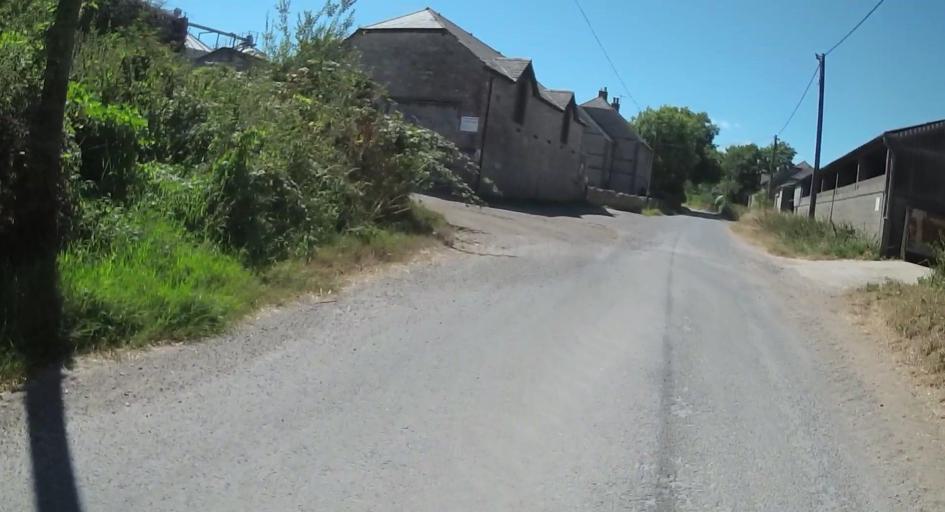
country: GB
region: England
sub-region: Dorset
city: Bovington Camp
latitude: 50.6503
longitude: -2.2936
